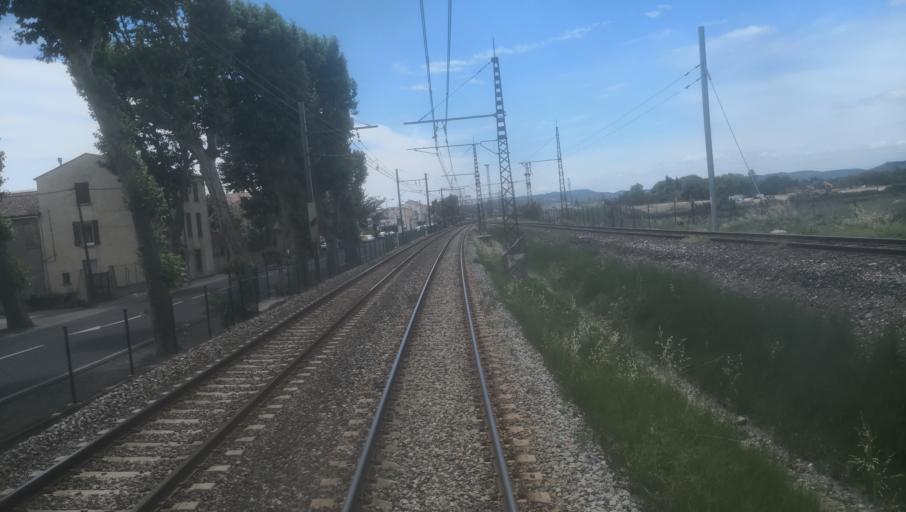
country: FR
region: Languedoc-Roussillon
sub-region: Departement de l'Aude
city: Narbonne
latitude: 43.1973
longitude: 3.0134
